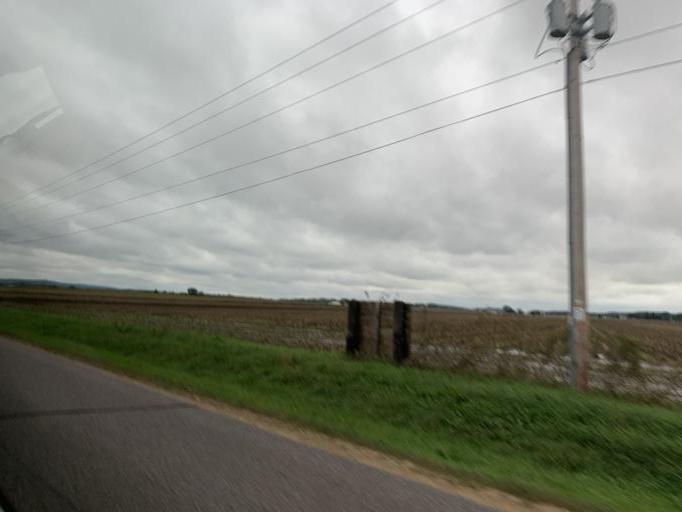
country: US
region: Wisconsin
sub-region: Sauk County
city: Prairie du Sac
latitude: 43.3166
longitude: -89.7763
